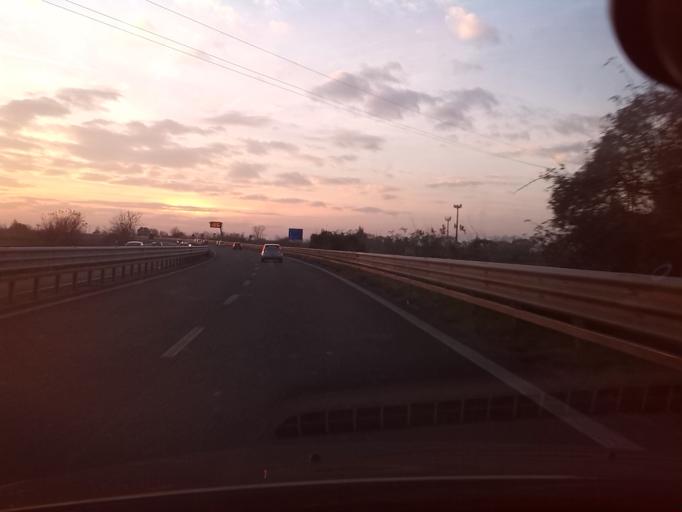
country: IT
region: Friuli Venezia Giulia
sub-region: Provincia di Udine
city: Basaldella
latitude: 46.0179
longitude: 13.2329
